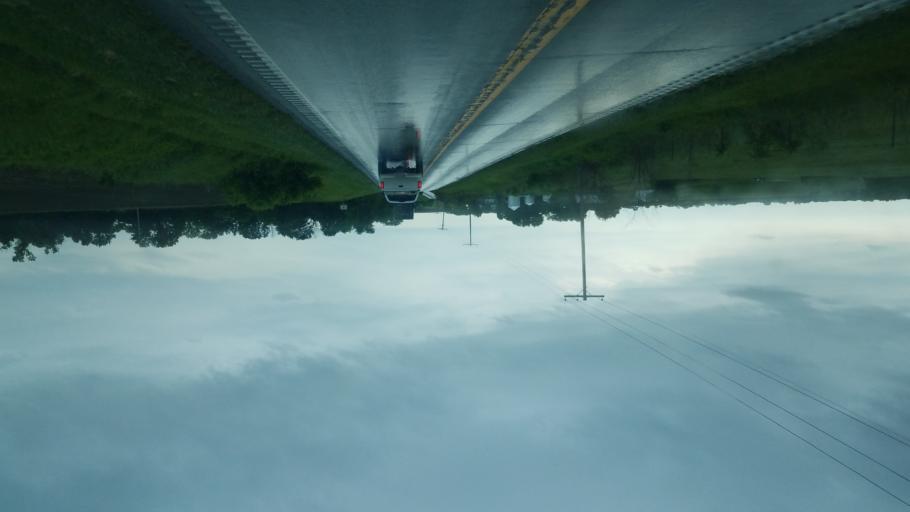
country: US
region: Missouri
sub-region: Cooper County
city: Boonville
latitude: 38.8820
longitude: -92.6509
